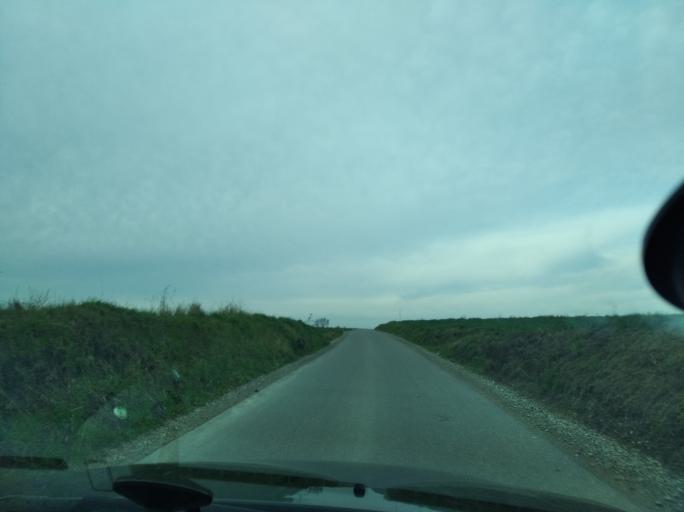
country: PL
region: Subcarpathian Voivodeship
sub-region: Powiat przeworski
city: Grzeska
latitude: 50.0676
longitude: 22.4629
